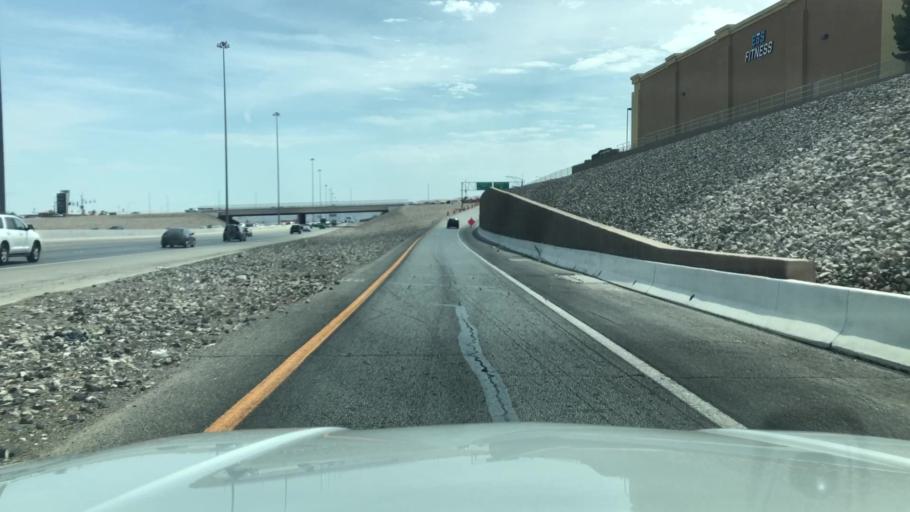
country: US
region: Nevada
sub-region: Clark County
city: Whitney
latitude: 36.0286
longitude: -115.0514
